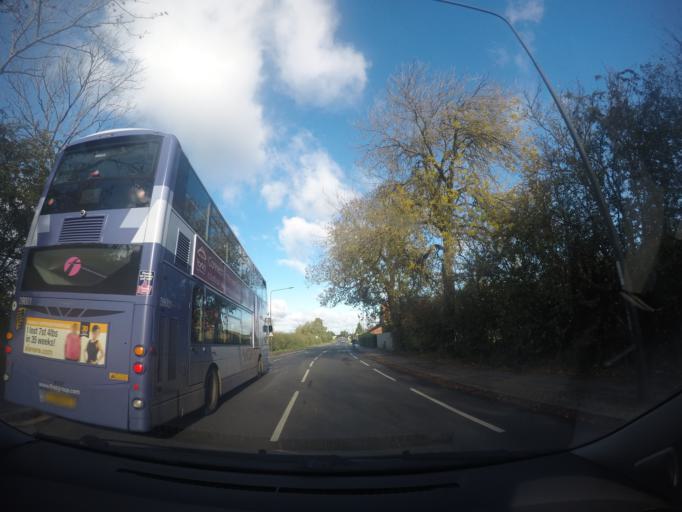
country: GB
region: England
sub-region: City of York
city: Haxby
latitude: 53.9984
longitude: -1.0724
